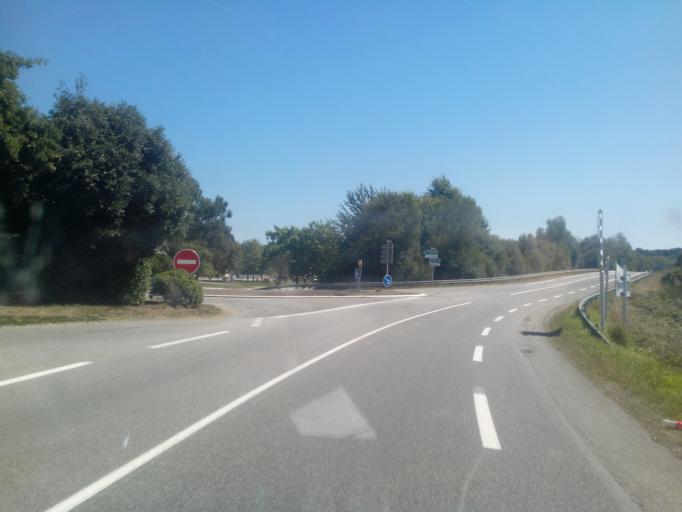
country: FR
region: Brittany
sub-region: Departement du Morbihan
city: Guegon
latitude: 47.9578
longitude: -2.5710
